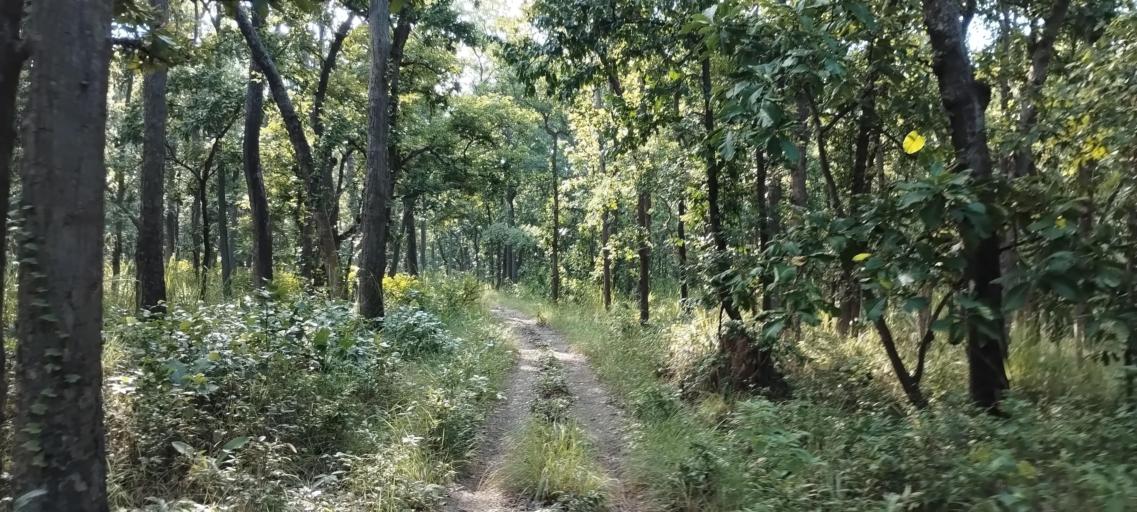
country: NP
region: Far Western
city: Tikapur
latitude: 28.5223
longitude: 81.2705
